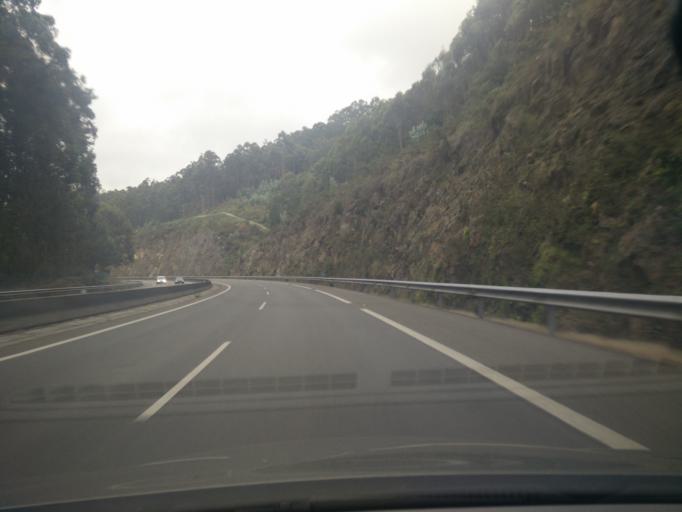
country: ES
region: Galicia
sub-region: Provincia da Coruna
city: Arteixo
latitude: 43.2811
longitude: -8.5158
